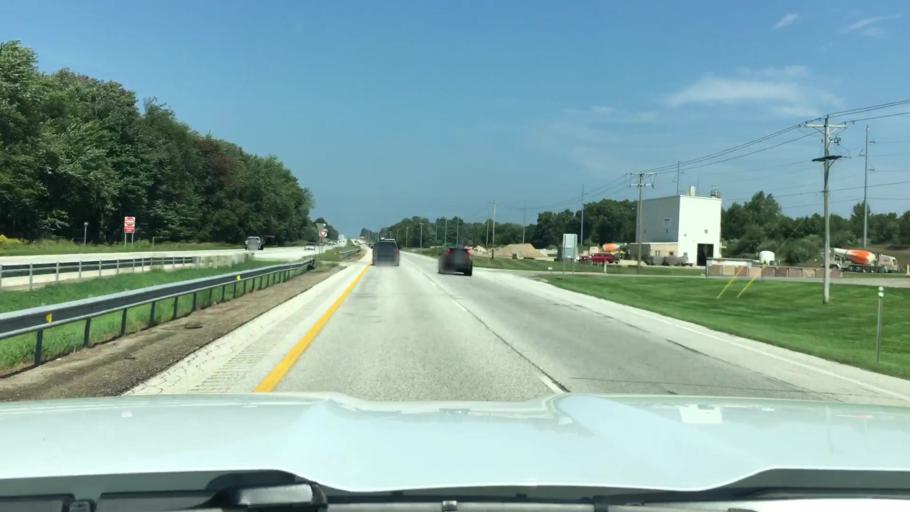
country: US
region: Michigan
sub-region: Kalamazoo County
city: Schoolcraft
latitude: 42.0489
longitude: -85.6356
